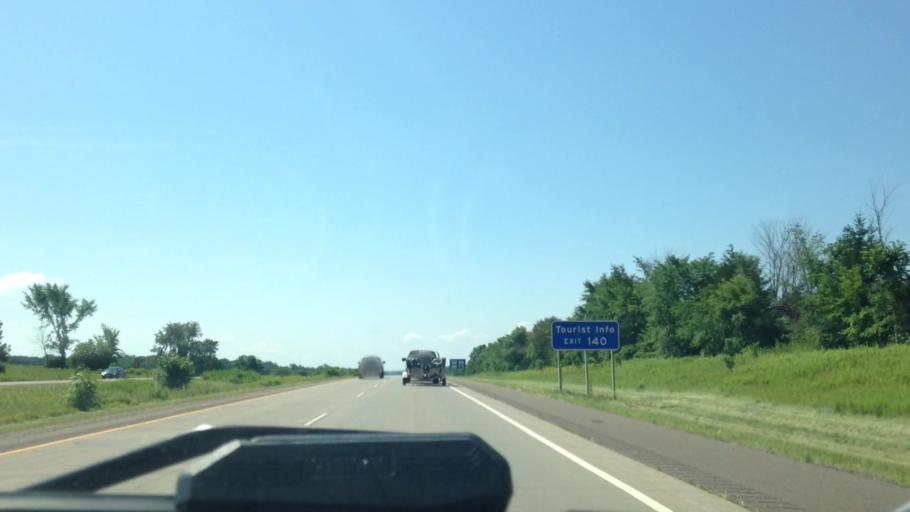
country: US
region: Wisconsin
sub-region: Barron County
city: Rice Lake
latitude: 45.4873
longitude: -91.7624
